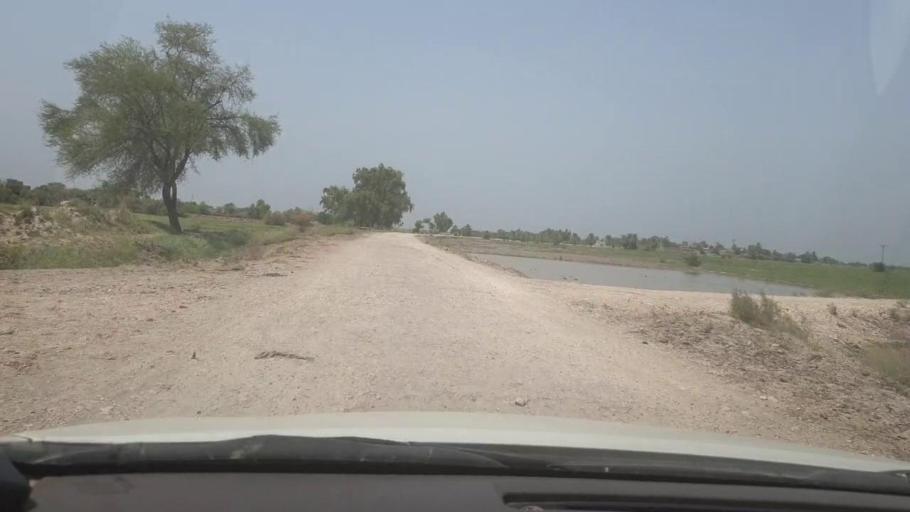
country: PK
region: Sindh
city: Shikarpur
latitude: 27.9424
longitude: 68.5726
